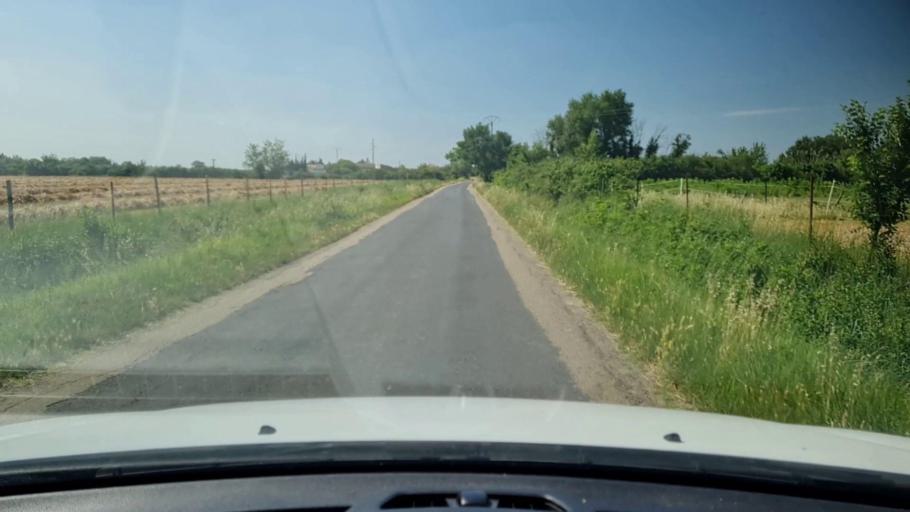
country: FR
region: Languedoc-Roussillon
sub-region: Departement du Gard
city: Le Cailar
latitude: 43.6654
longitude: 4.2315
